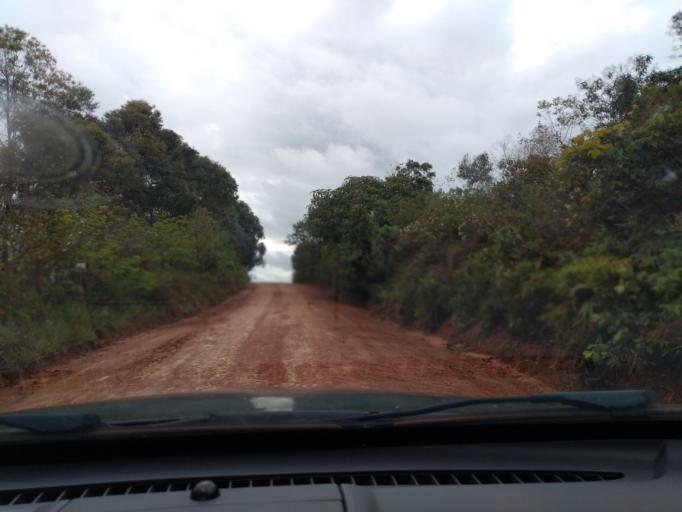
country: BR
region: Minas Gerais
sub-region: Lavras
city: Lavras
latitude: -21.5106
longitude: -44.9269
